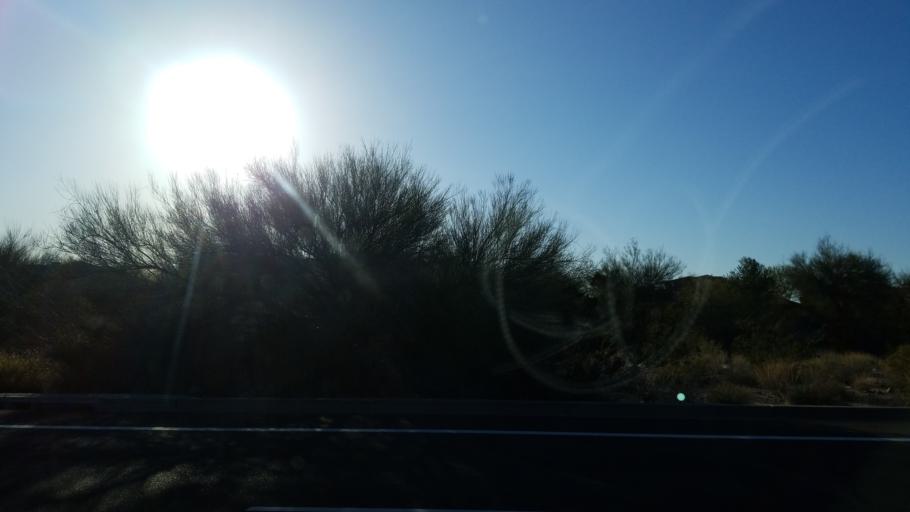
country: US
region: Arizona
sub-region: Maricopa County
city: Paradise Valley
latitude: 33.6682
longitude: -111.8907
